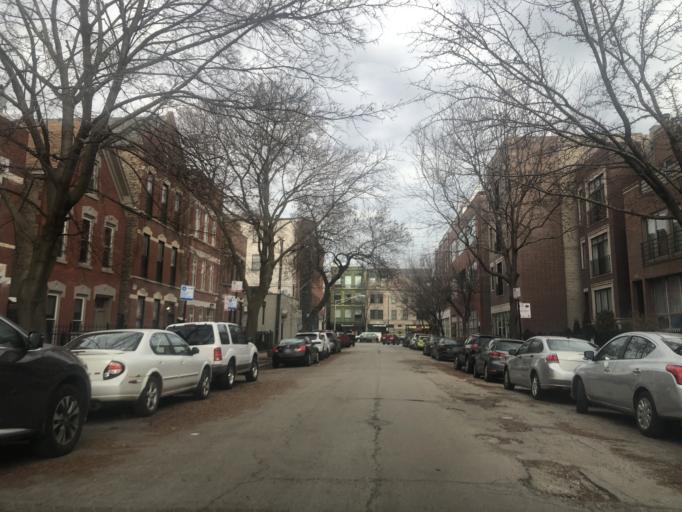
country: US
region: Illinois
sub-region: Cook County
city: Chicago
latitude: 41.9023
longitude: -87.6711
